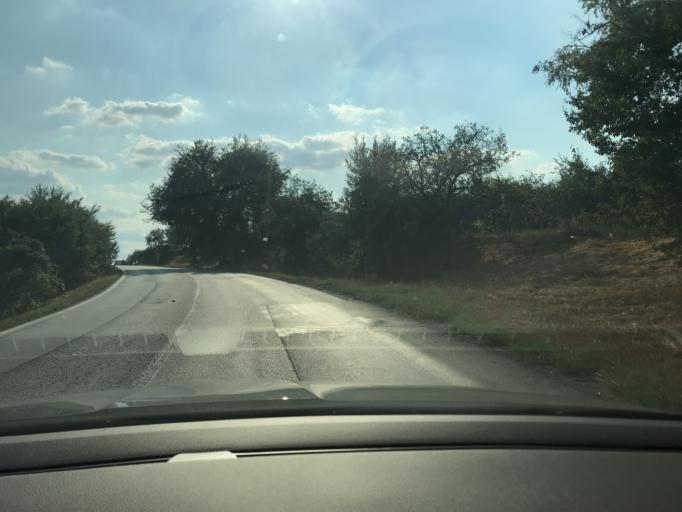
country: CZ
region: Central Bohemia
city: Velvary
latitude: 50.2598
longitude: 14.1727
